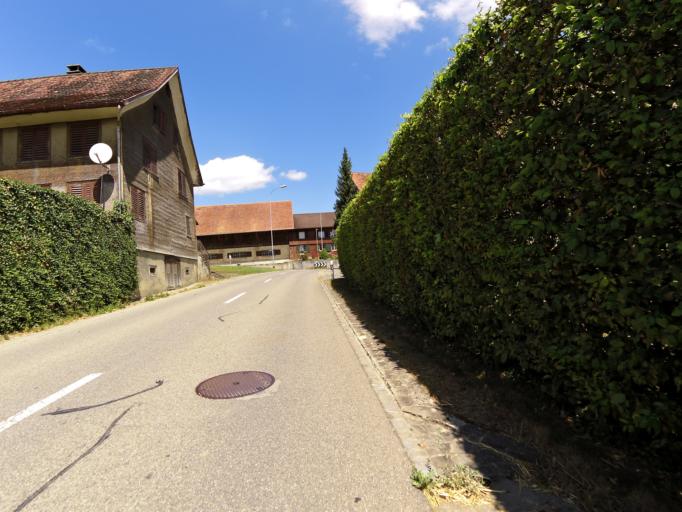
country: CH
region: Thurgau
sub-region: Weinfelden District
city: Maerstetten-Dorf
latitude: 47.6071
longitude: 9.0637
